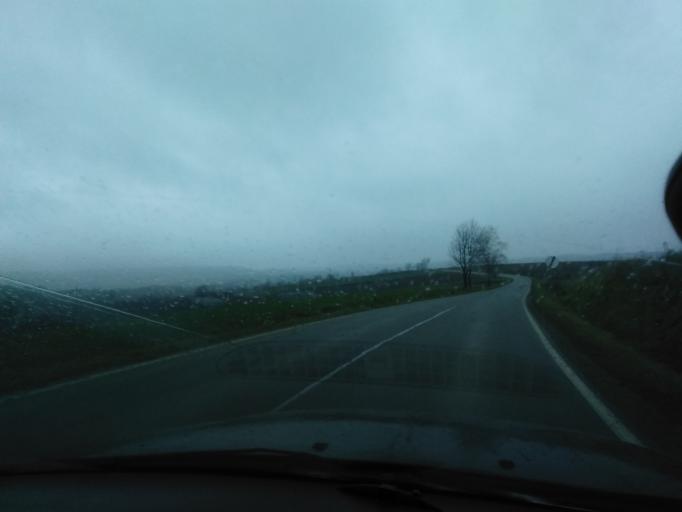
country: PL
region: Subcarpathian Voivodeship
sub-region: Powiat jaroslawski
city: Rokietnica
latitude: 49.9018
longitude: 22.5831
